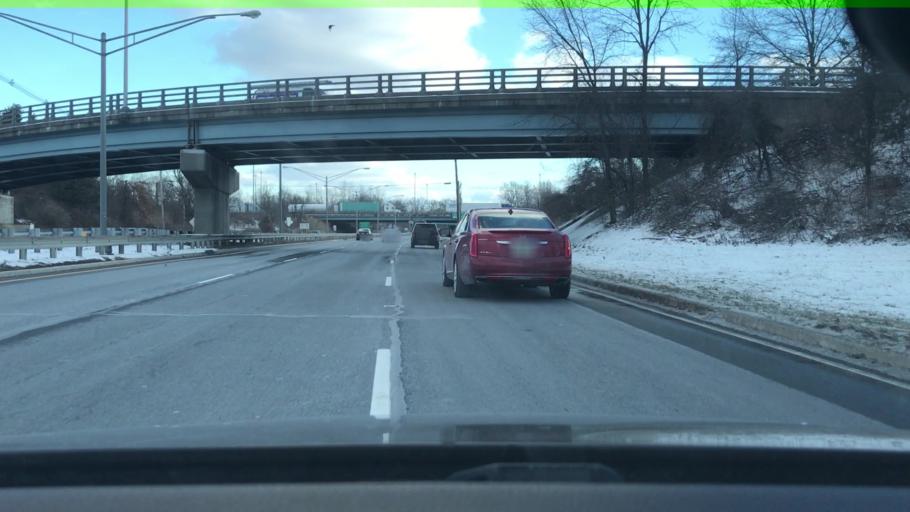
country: US
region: New Jersey
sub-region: Morris County
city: Parsippany
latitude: 40.8339
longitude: -74.4410
